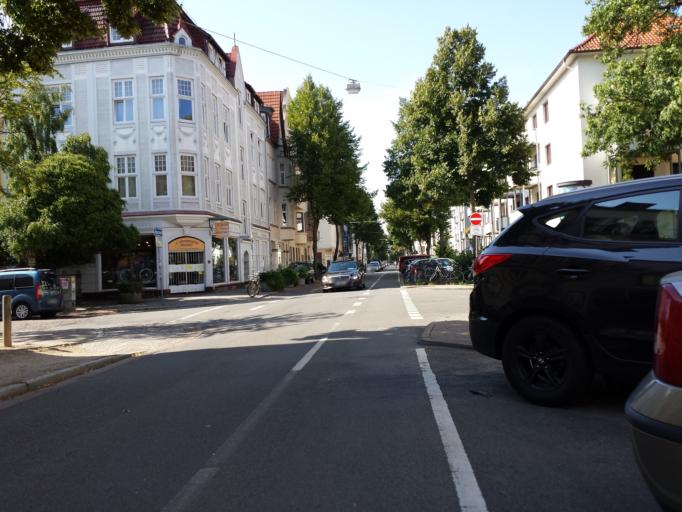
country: DE
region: Bremen
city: Bremen
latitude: 53.0690
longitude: 8.7931
